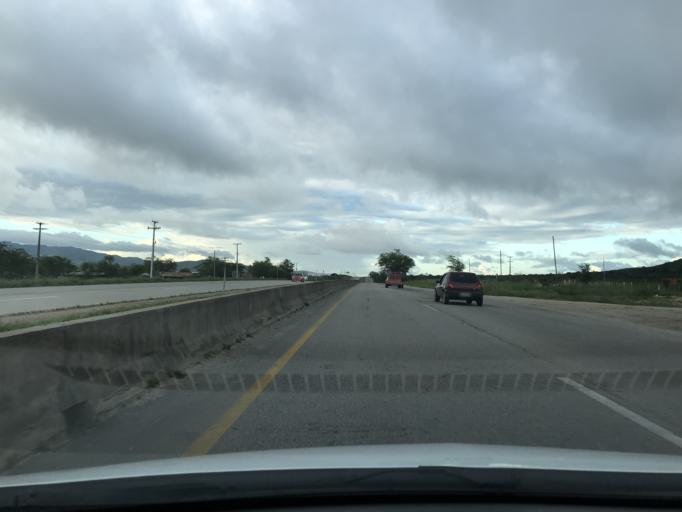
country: BR
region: Pernambuco
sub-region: Bezerros
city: Bezerros
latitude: -8.2861
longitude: -35.8170
